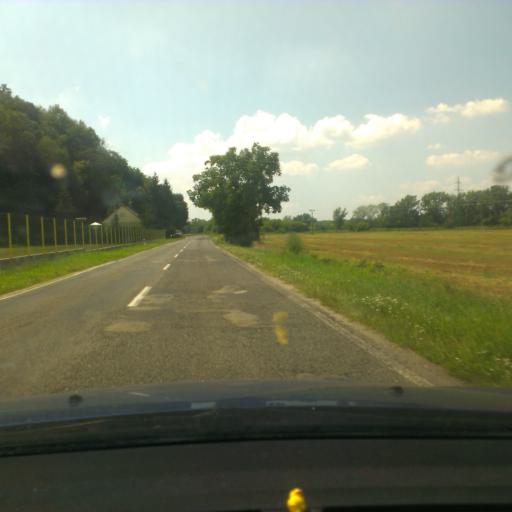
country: SK
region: Trnavsky
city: Hlohovec
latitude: 48.5043
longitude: 17.8244
